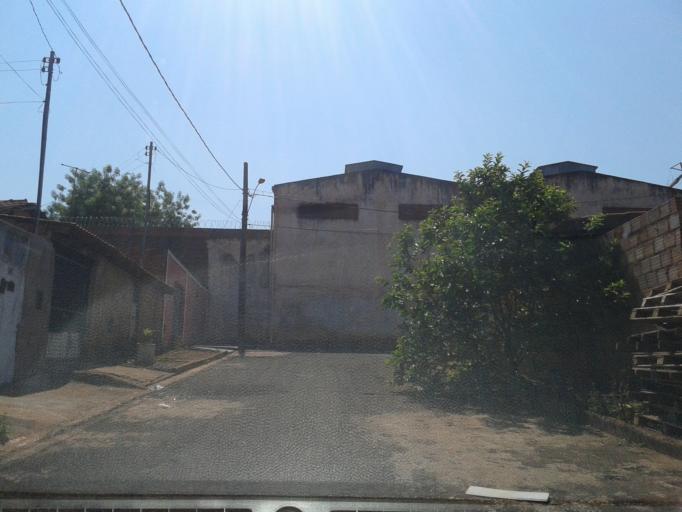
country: BR
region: Minas Gerais
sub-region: Ituiutaba
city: Ituiutaba
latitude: -18.9547
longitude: -49.4547
